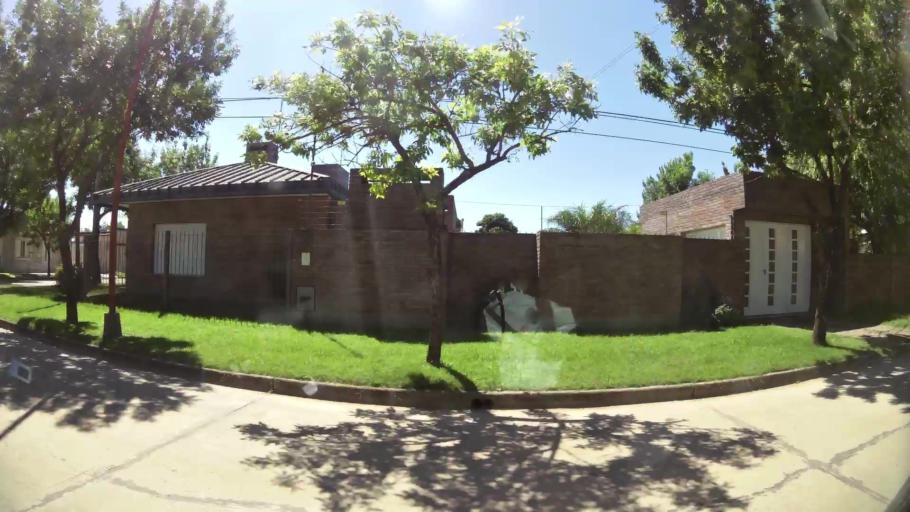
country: AR
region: Santa Fe
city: Esperanza
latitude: -31.4383
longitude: -60.9300
